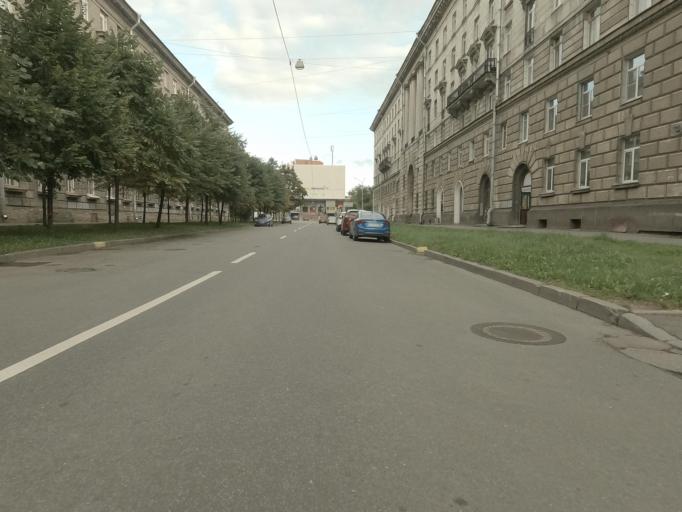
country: RU
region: St.-Petersburg
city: Avtovo
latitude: 59.8686
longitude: 30.2661
